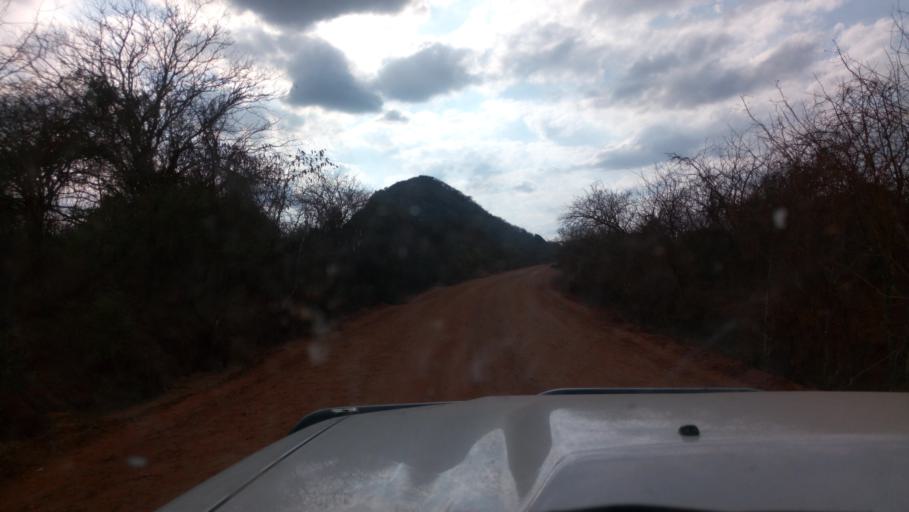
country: KE
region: Kitui
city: Kitui
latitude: -1.7082
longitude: 38.3695
